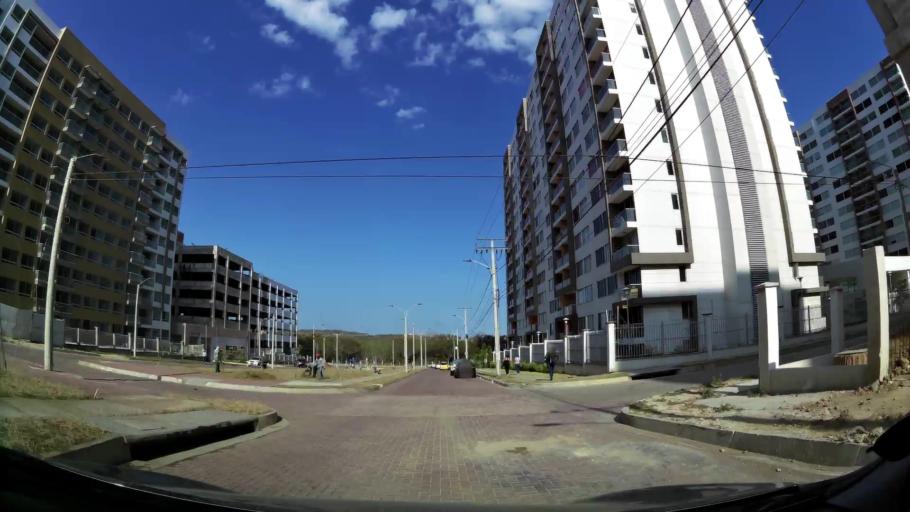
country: CO
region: Atlantico
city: Barranquilla
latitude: 11.0083
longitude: -74.8369
